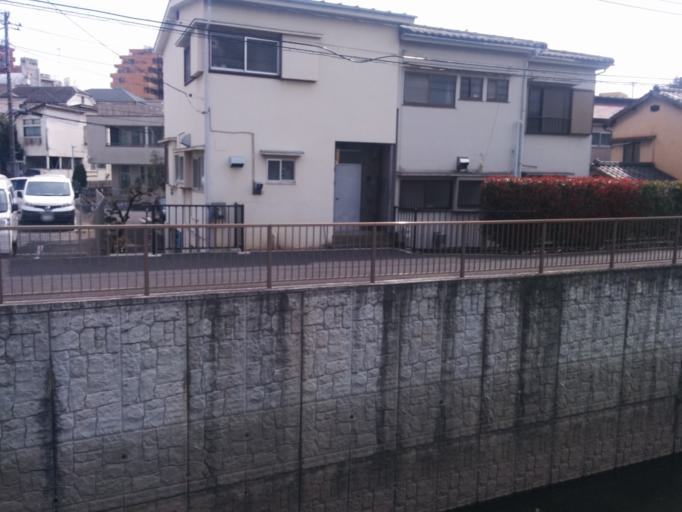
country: JP
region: Tokyo
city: Tokyo
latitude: 35.6859
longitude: 139.6553
